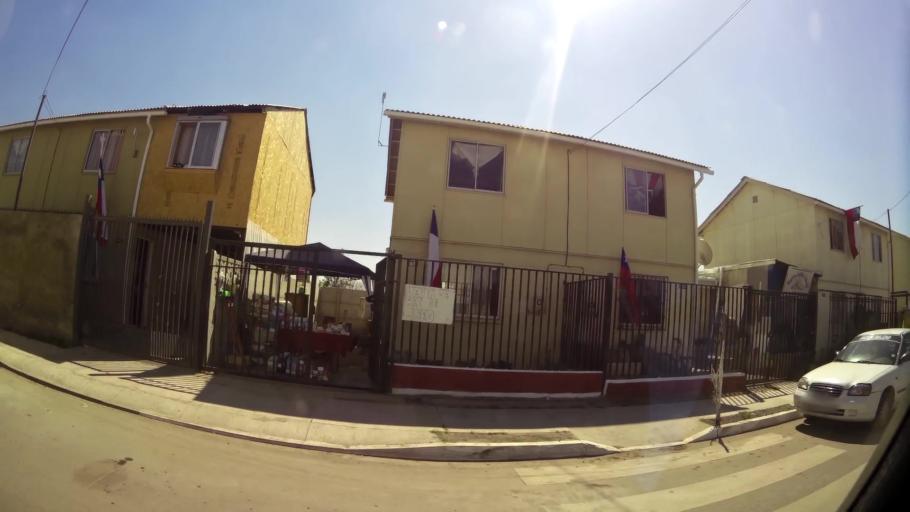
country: CL
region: Santiago Metropolitan
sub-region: Provincia de Talagante
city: Penaflor
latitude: -33.5819
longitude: -70.8068
